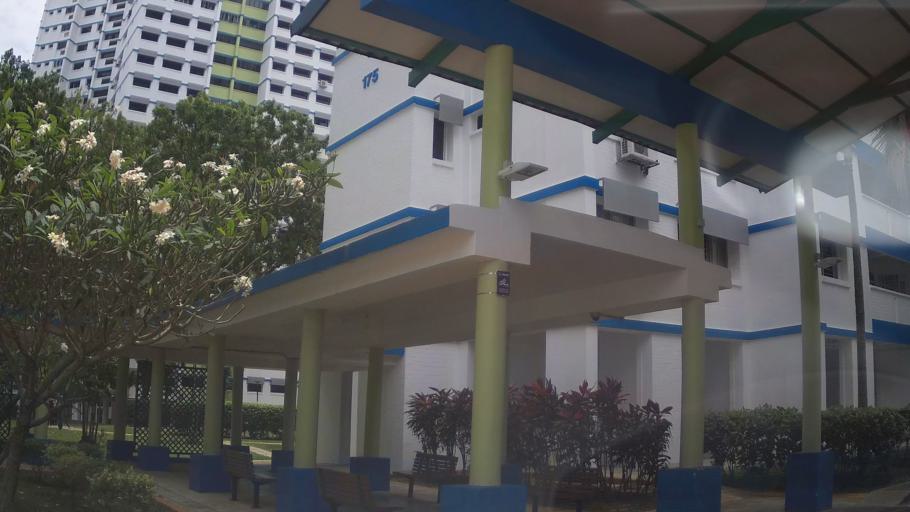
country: MY
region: Johor
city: Johor Bahru
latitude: 1.3801
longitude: 103.7660
